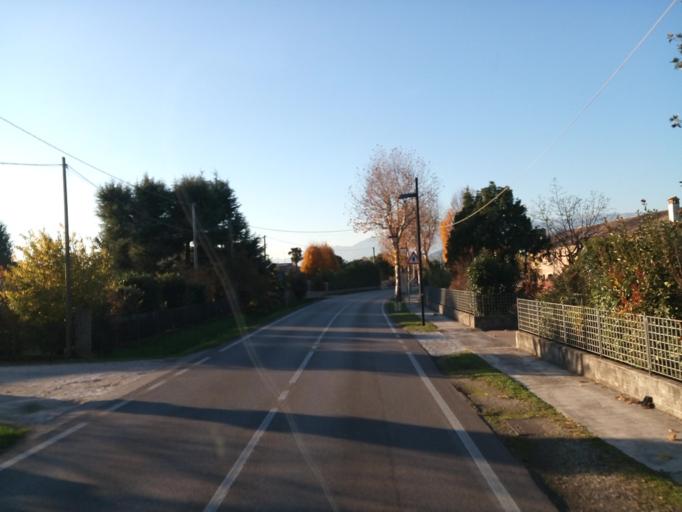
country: IT
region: Veneto
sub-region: Provincia di Treviso
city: Caerano di San Marco
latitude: 45.7881
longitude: 11.9877
